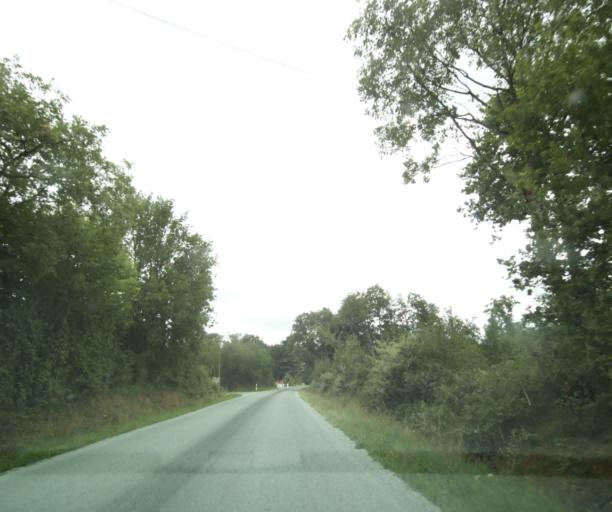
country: FR
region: Pays de la Loire
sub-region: Departement de Maine-et-Loire
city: Durtal
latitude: 47.7078
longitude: -0.2686
